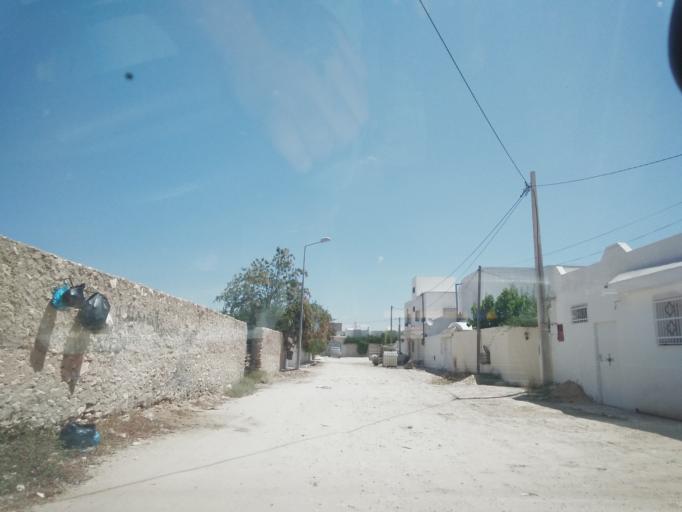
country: TN
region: Safaqis
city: Al Qarmadah
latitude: 34.8225
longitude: 10.7646
